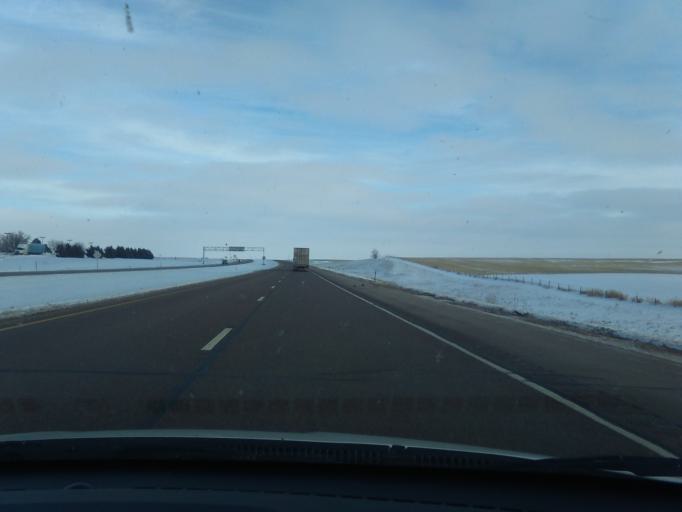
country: US
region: Nebraska
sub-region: Cheyenne County
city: Sidney
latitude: 41.1127
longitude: -102.9280
